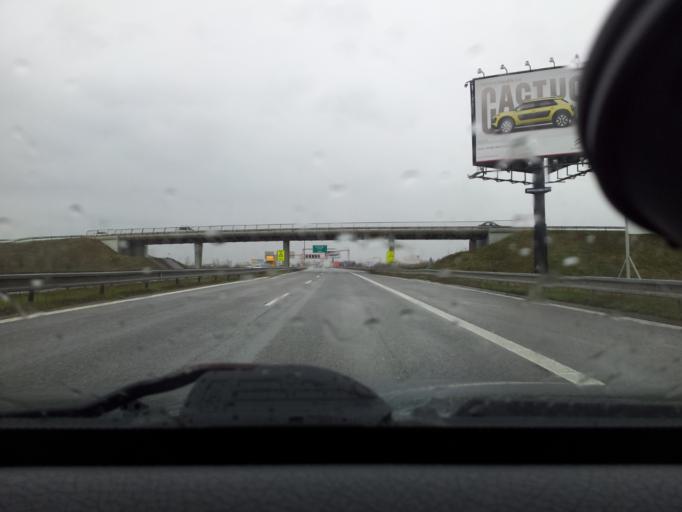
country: SK
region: Bratislavsky
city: Svaty Jur
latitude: 48.1866
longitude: 17.2028
